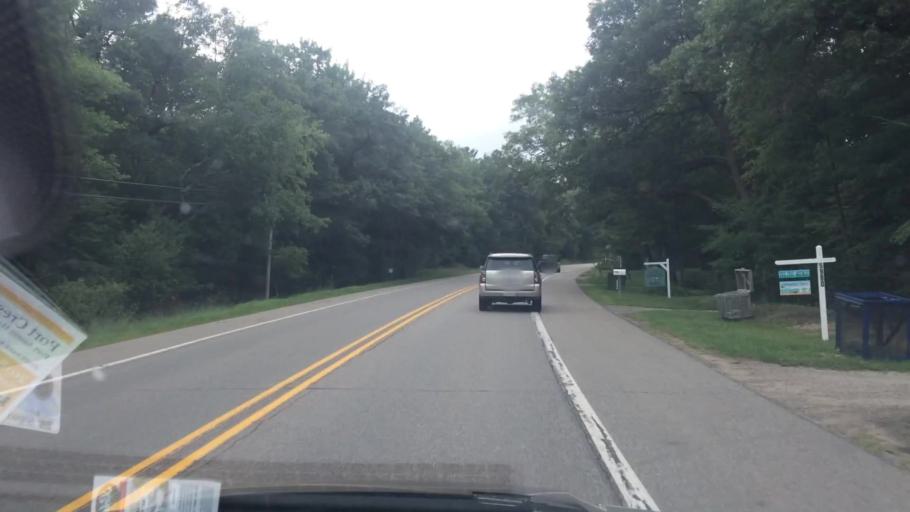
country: US
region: Michigan
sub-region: Huron County
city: Pigeon
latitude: 43.9695
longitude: -83.2600
